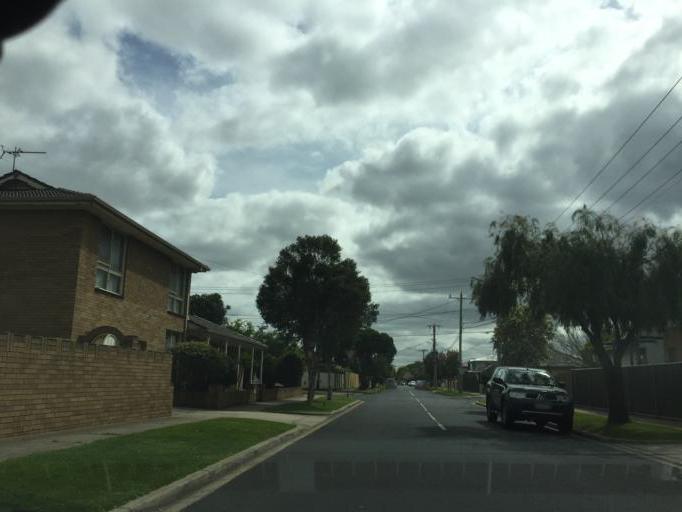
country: AU
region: Victoria
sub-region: Maribyrnong
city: Kingsville
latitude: -37.8151
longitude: 144.8667
